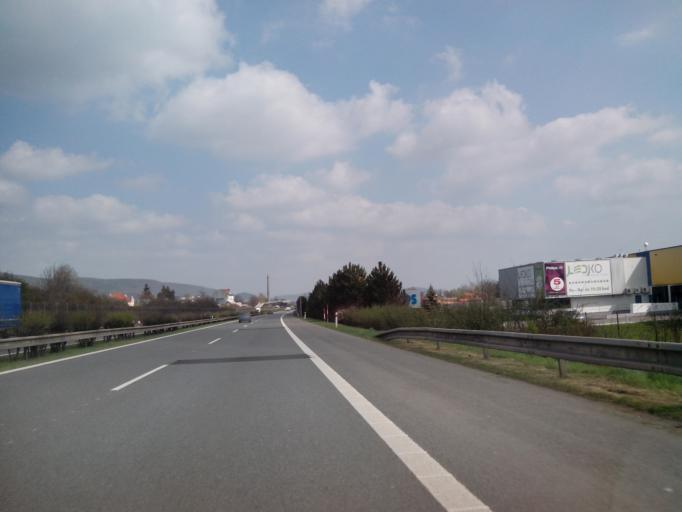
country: CZ
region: Central Bohemia
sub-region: Okres Beroun
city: Kraluv Dvur
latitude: 49.9387
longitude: 14.0250
